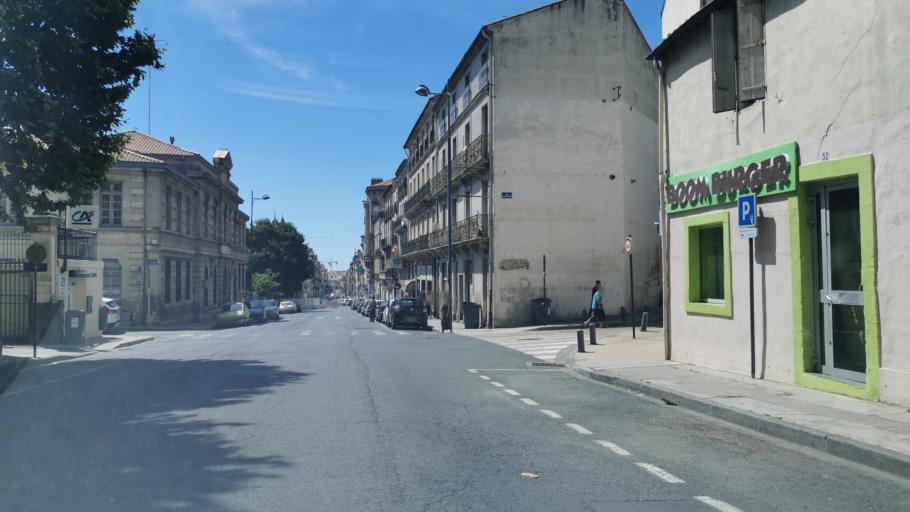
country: FR
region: Languedoc-Roussillon
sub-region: Departement de l'Herault
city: Beziers
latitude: 43.3459
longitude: 3.2193
